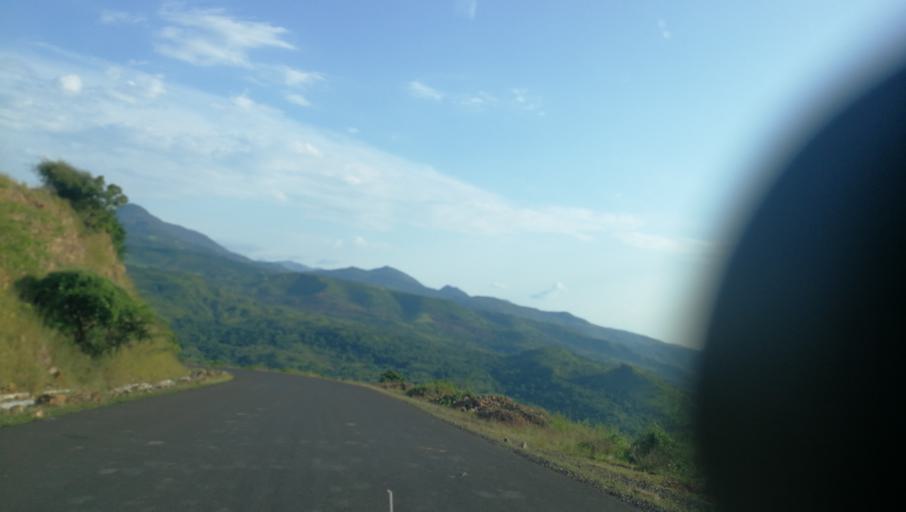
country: ET
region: Southern Nations, Nationalities, and People's Region
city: Areka
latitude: 6.8286
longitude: 37.3015
